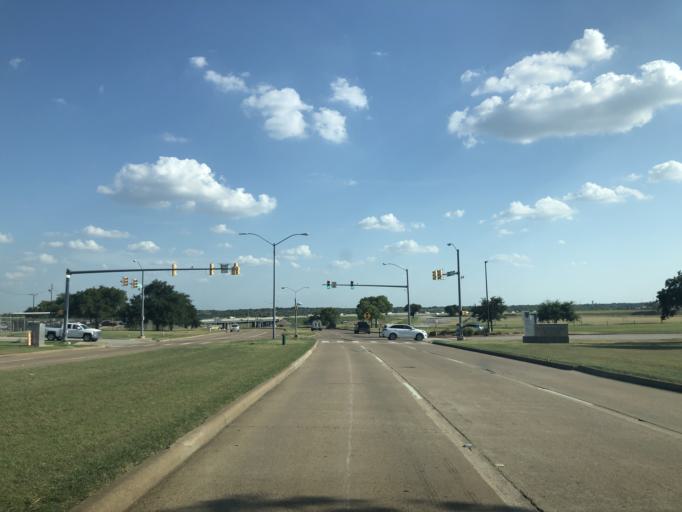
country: US
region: Texas
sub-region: Tarrant County
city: Sansom Park
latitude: 32.8304
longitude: -97.3857
